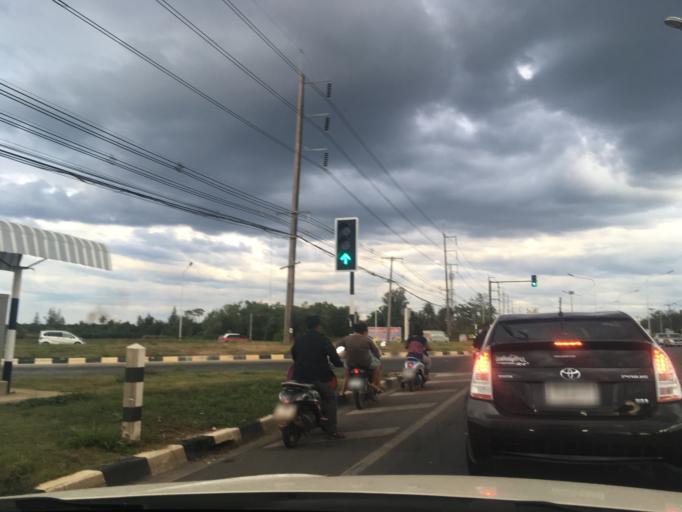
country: TH
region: Rayong
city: Klaeng
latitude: 12.7859
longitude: 101.6771
